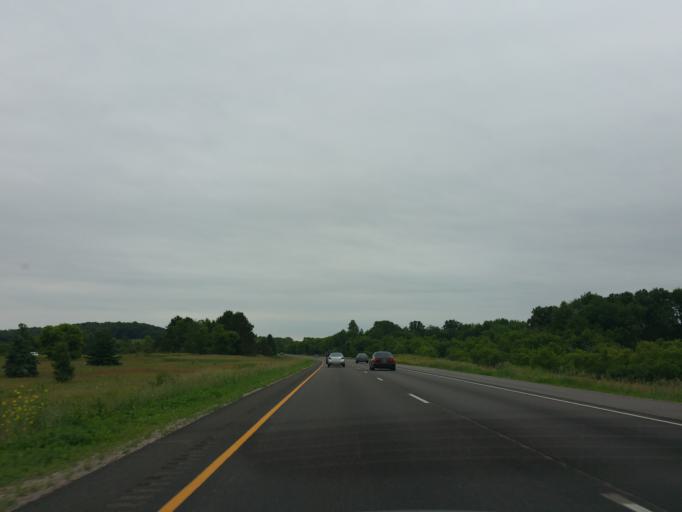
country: US
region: Wisconsin
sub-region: Eau Claire County
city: Fall Creek
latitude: 44.7002
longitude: -91.3418
